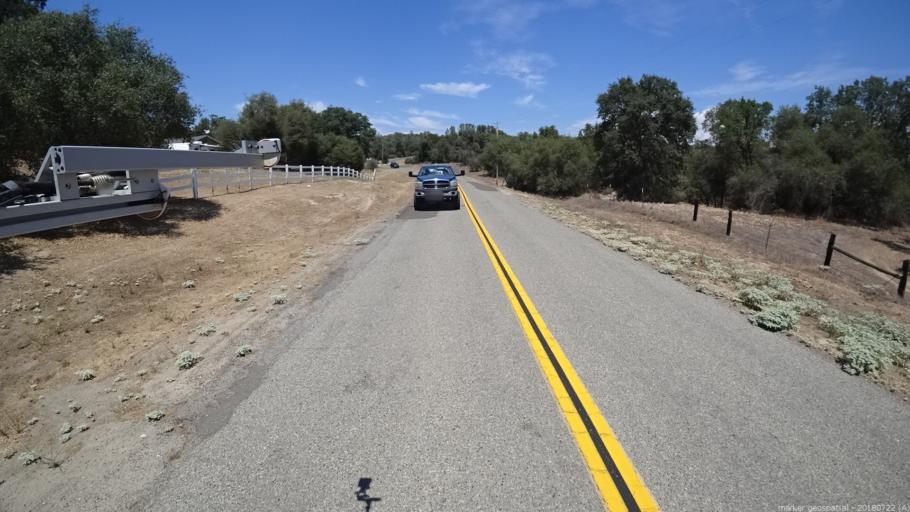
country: US
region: California
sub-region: Madera County
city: Yosemite Lakes
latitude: 37.2135
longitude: -119.7291
